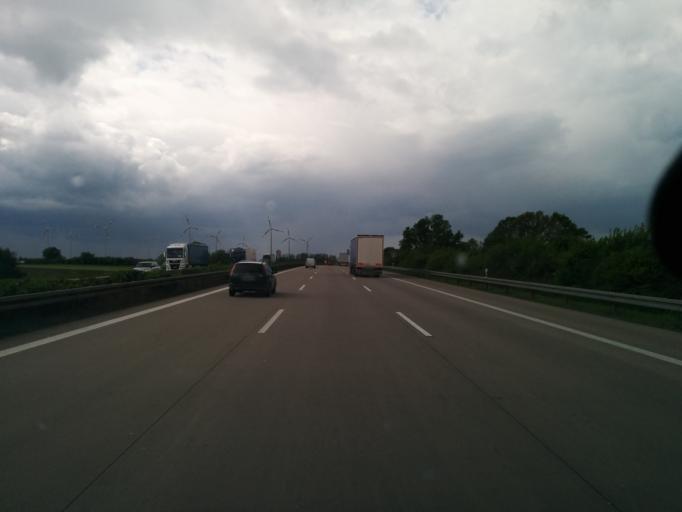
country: DE
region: Saxony-Anhalt
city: Erxleben
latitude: 52.1913
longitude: 11.3063
